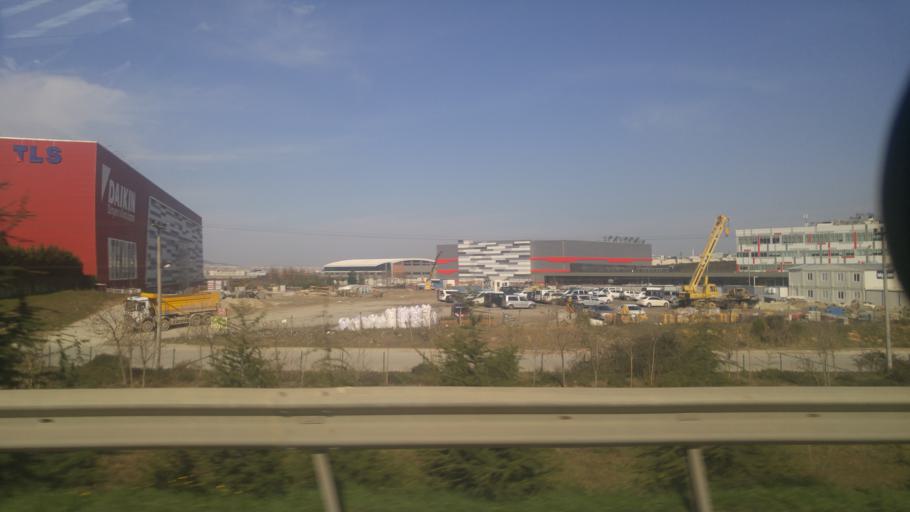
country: TR
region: Kocaeli
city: Balcik
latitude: 40.8680
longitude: 29.3906
